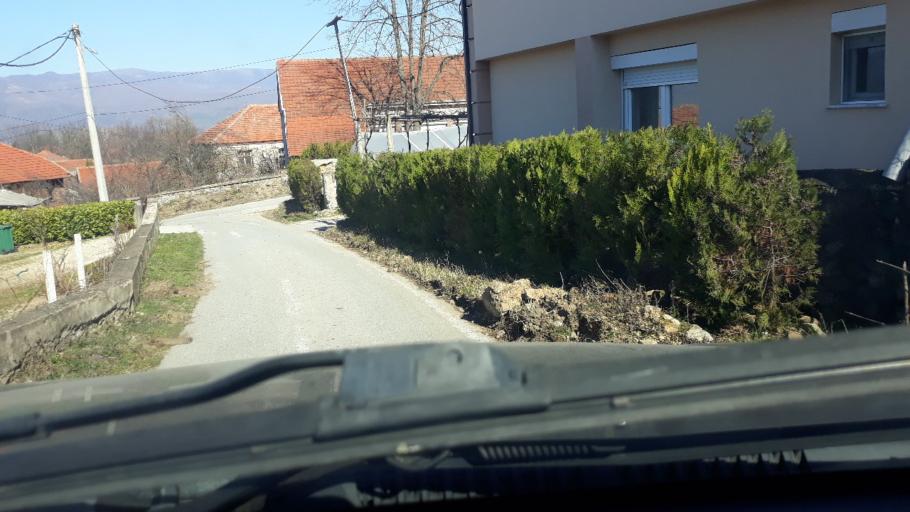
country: MK
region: Bosilovo
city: Sekirnik
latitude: 41.3787
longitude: 22.8137
